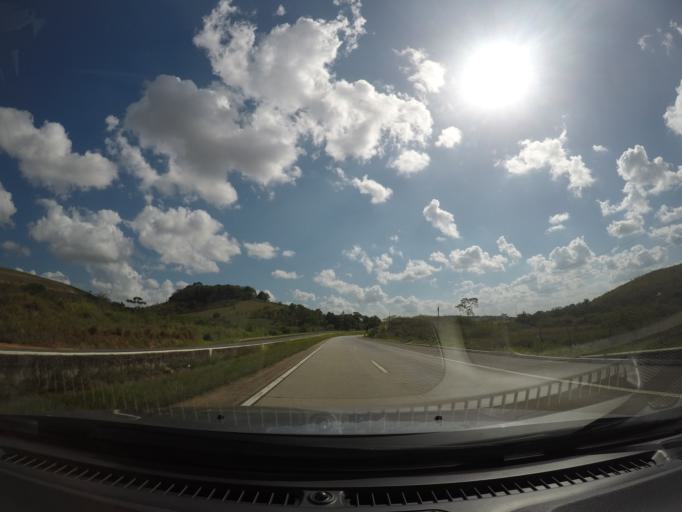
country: BR
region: Pernambuco
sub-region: Ribeirao
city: Ribeirao
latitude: -8.4421
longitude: -35.3370
